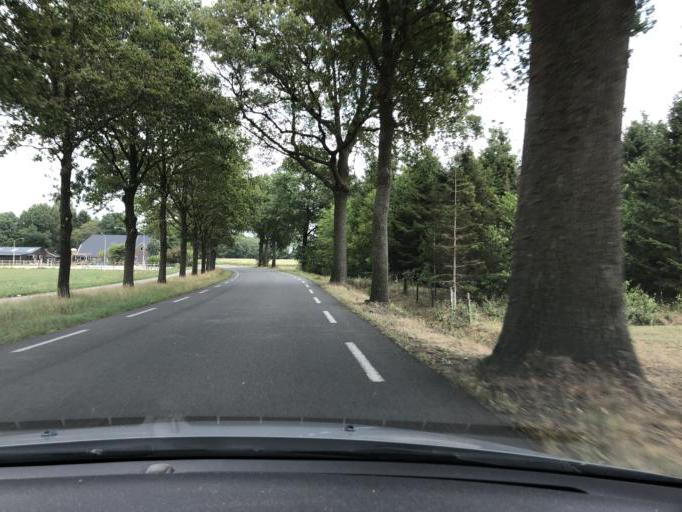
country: NL
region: Drenthe
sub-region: Gemeente Borger-Odoorn
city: Borger
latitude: 52.9017
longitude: 6.6909
